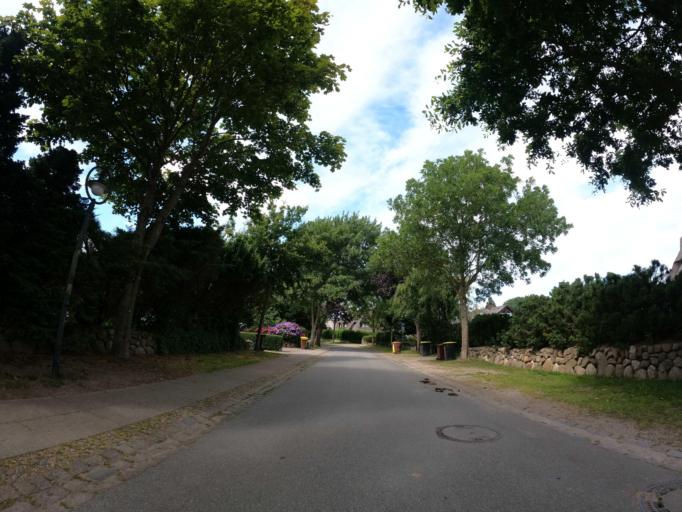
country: DE
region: Schleswig-Holstein
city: Keitum
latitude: 54.8892
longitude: 8.3725
